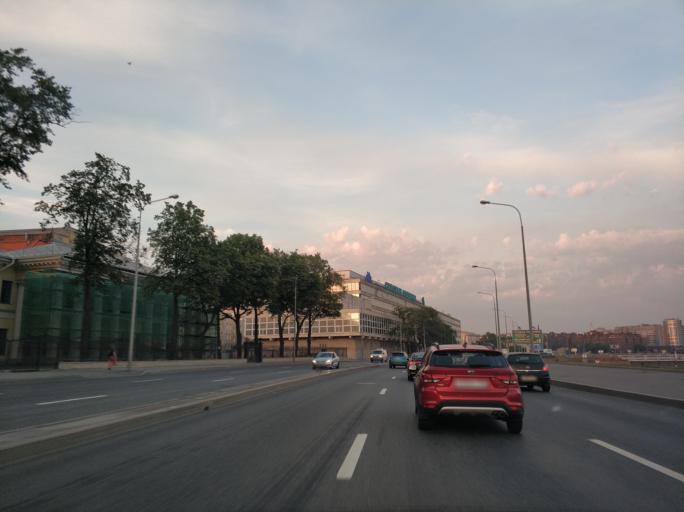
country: RU
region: Leningrad
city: Finlyandskiy
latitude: 59.9598
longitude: 30.3867
